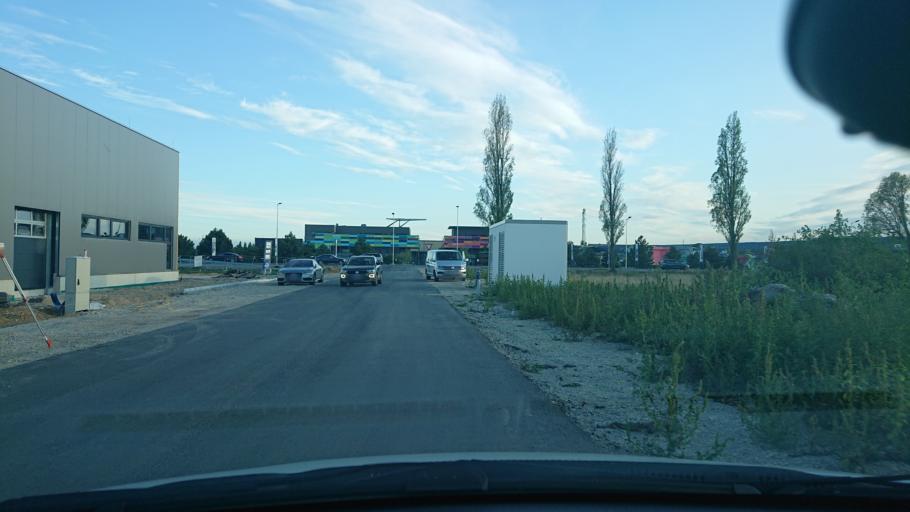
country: AT
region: Lower Austria
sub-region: Politischer Bezirk Baden
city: Leobersdorf
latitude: 47.9325
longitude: 16.2002
